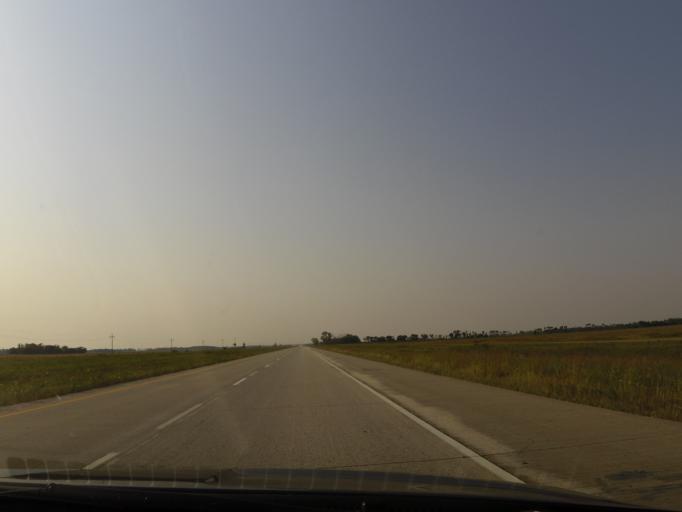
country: US
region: North Dakota
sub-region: Walsh County
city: Grafton
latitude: 48.2875
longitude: -97.1894
